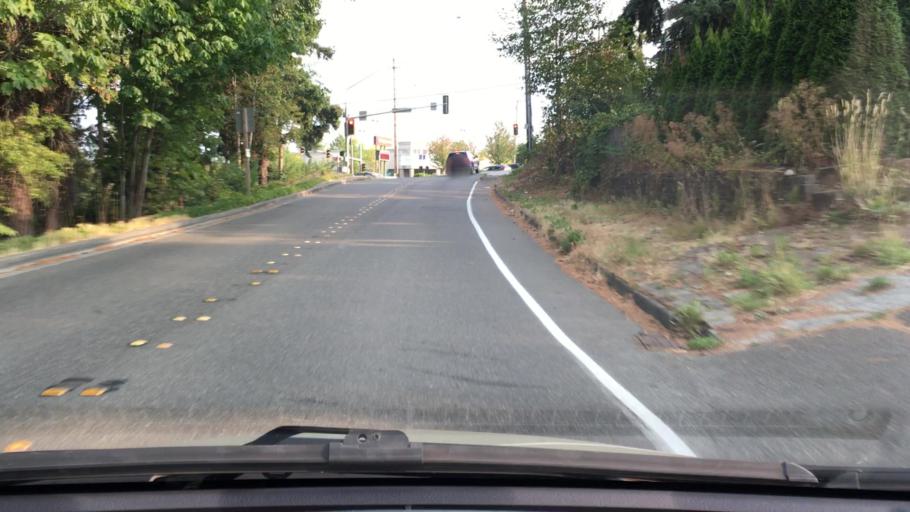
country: US
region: Washington
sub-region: Snohomish County
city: Martha Lake
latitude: 47.8503
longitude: -122.2475
